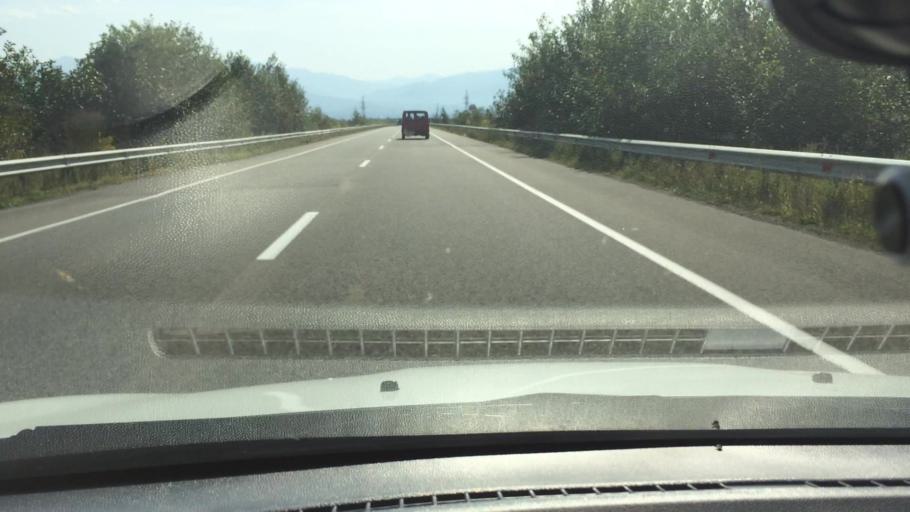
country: GE
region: Ajaria
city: Ochkhamuri
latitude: 41.9086
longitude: 41.7848
